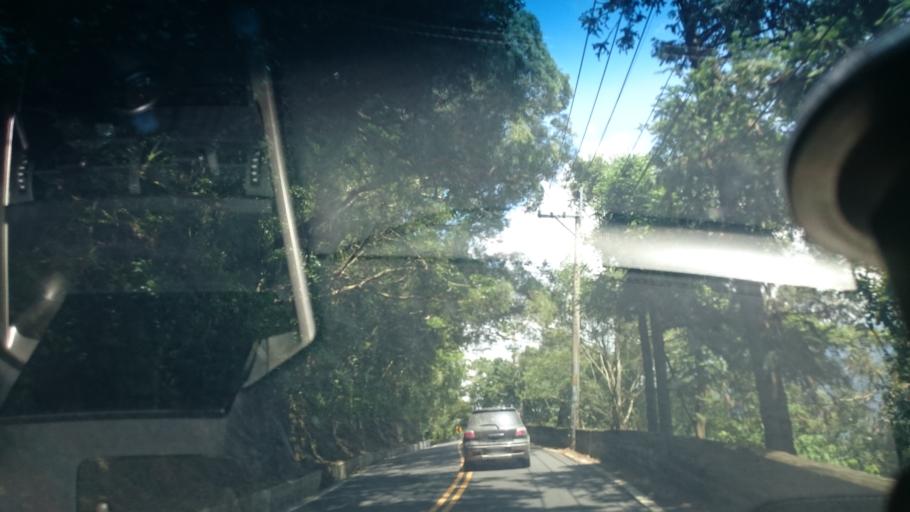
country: TW
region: Taiwan
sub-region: Nantou
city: Puli
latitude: 24.0267
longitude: 121.1379
